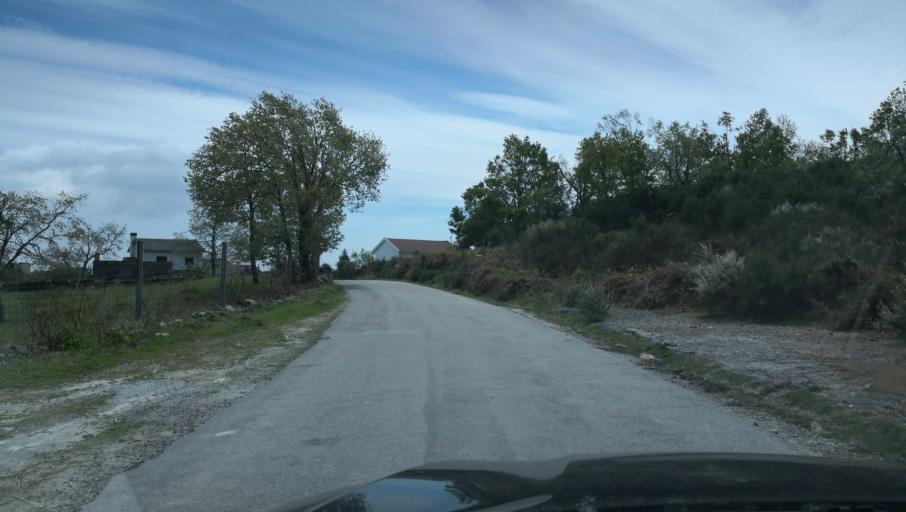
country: PT
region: Vila Real
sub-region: Vila Real
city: Vila Real
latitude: 41.2947
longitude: -7.8154
